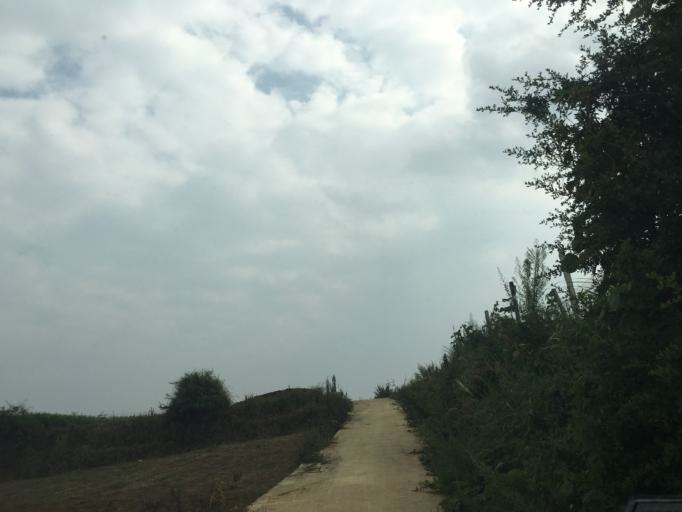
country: CN
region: Guangxi Zhuangzu Zizhiqu
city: Xinzhou
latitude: 25.4838
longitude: 105.6514
